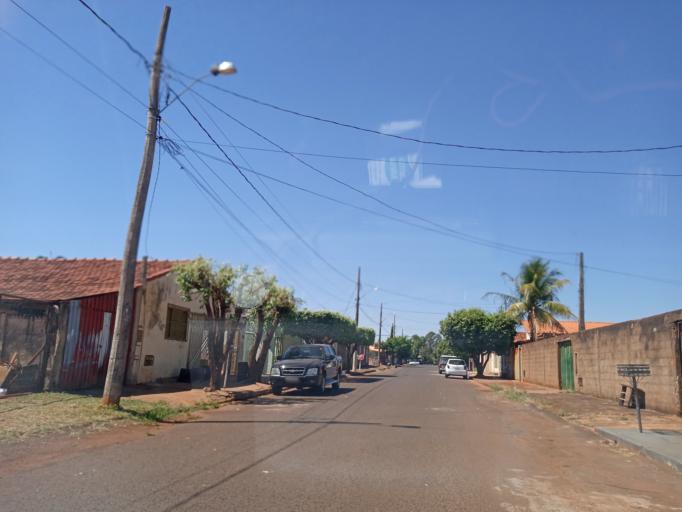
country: BR
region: Minas Gerais
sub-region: Ituiutaba
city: Ituiutaba
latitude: -18.9565
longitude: -49.4611
